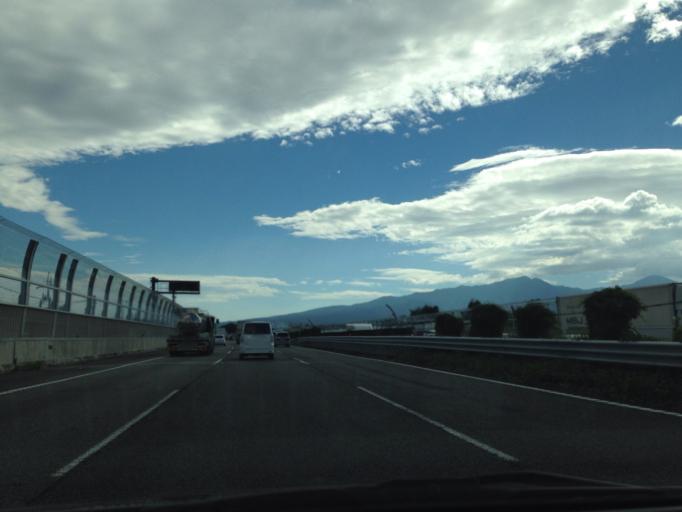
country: JP
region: Shizuoka
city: Gotemba
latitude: 35.2805
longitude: 138.9216
